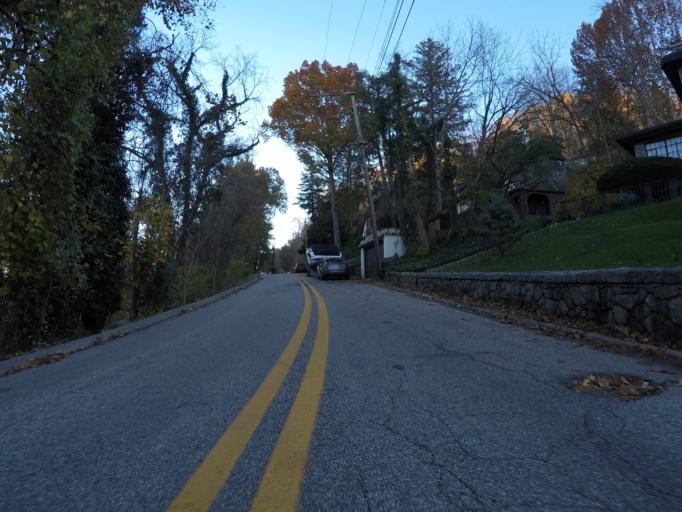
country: US
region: West Virginia
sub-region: Cabell County
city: Huntington
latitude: 38.4057
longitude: -82.4580
